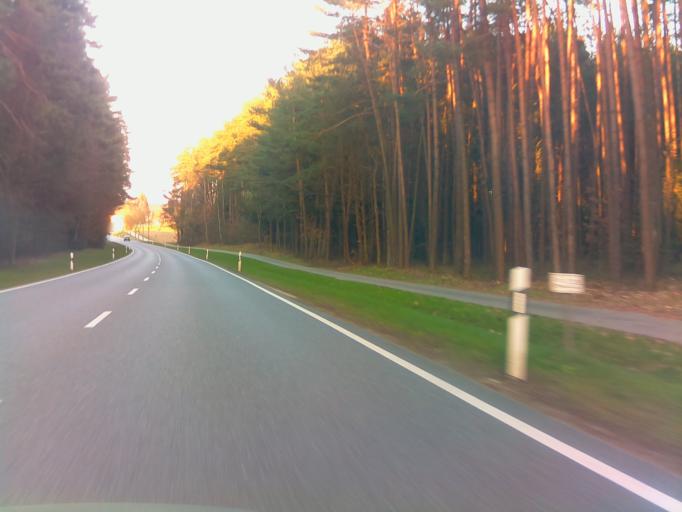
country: DE
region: Bavaria
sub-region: Lower Bavaria
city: Kirchdorf
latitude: 48.8094
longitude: 11.9188
